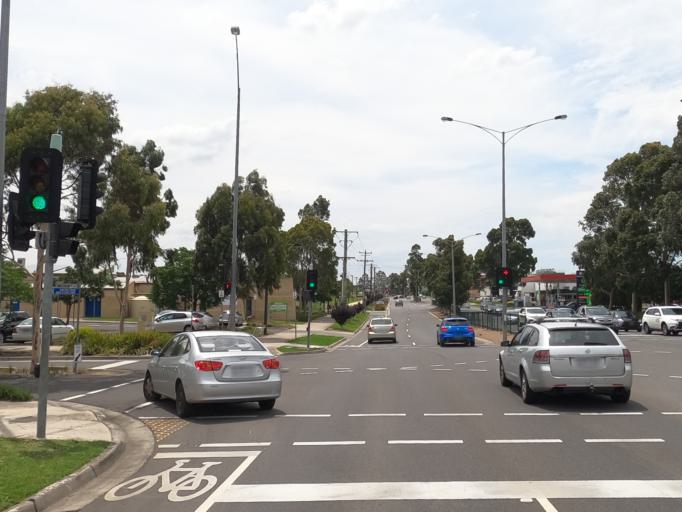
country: AU
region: Victoria
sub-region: Hume
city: Broadmeadows
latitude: -37.6810
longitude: 144.9165
